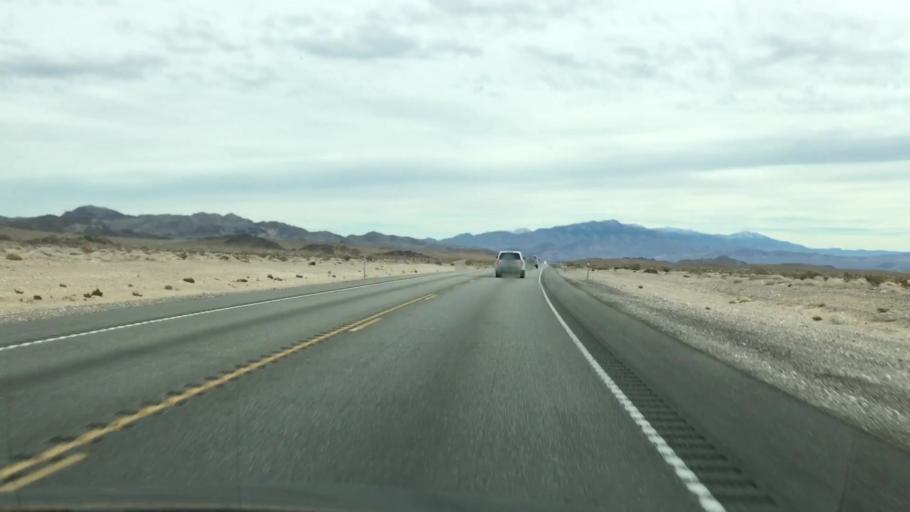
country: US
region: Nevada
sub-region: Nye County
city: Pahrump
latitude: 36.6228
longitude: -116.2988
